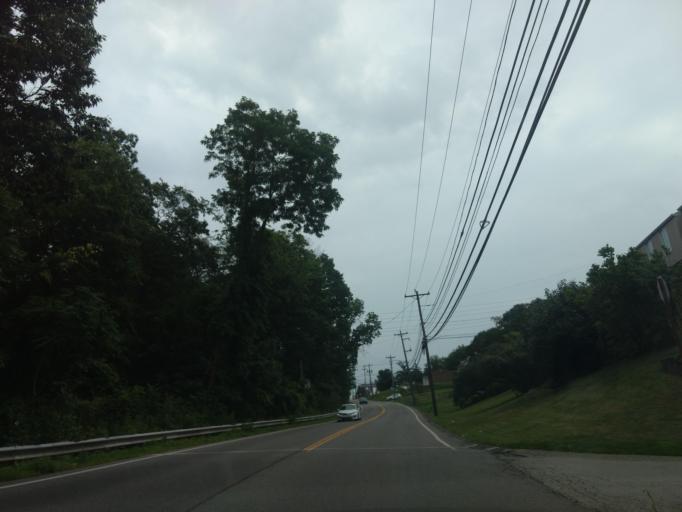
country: US
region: Pennsylvania
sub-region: Allegheny County
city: McKees Rocks
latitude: 40.4691
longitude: -80.1031
